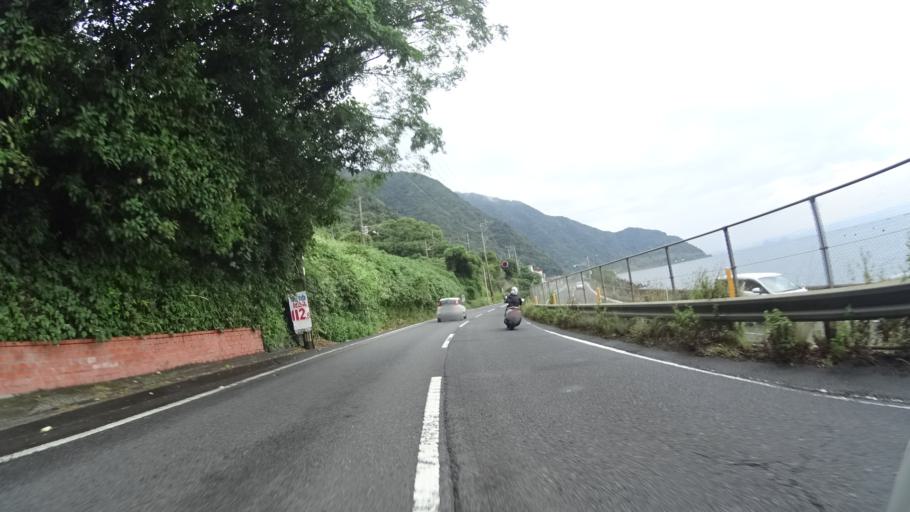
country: JP
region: Kagoshima
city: Kagoshima-shi
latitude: 31.6448
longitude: 130.6030
